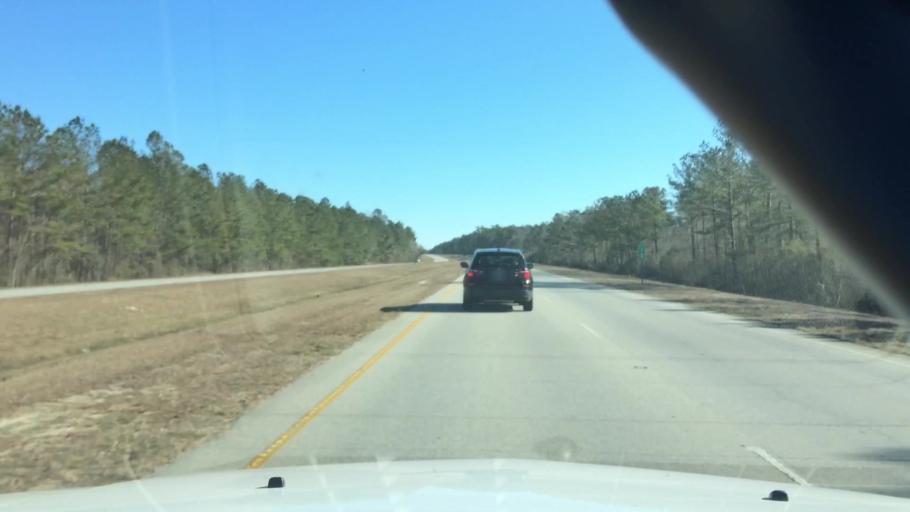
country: US
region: North Carolina
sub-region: Brunswick County
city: Bolivia
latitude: 34.0658
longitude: -78.1863
